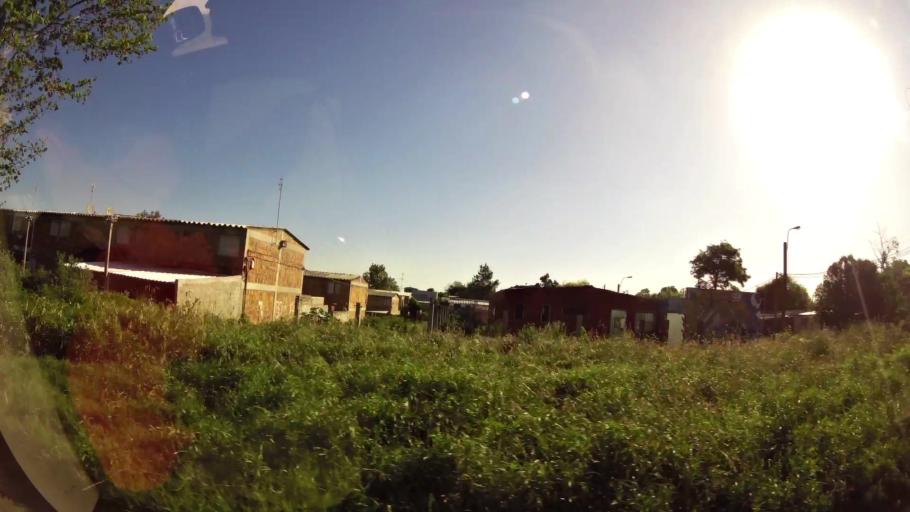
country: UY
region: Canelones
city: La Paz
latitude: -34.8126
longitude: -56.2253
